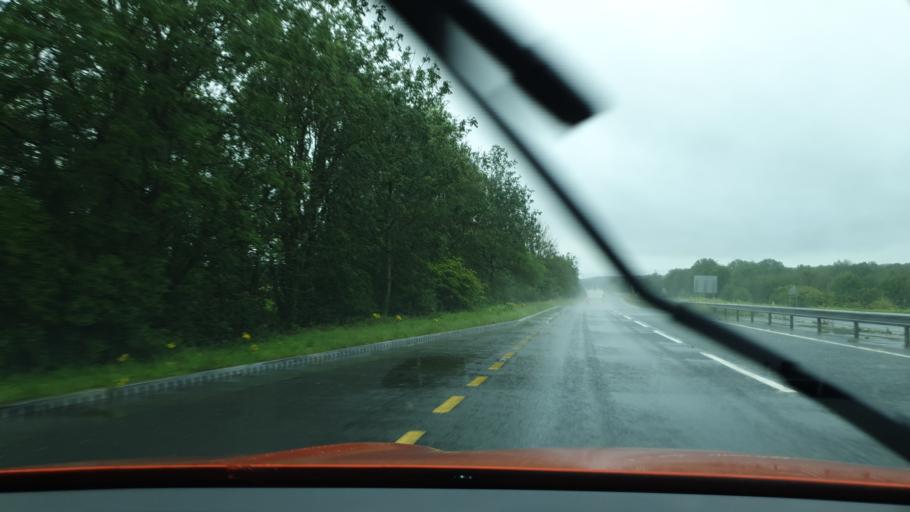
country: GB
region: England
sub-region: Cumbria
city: Arnside
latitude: 54.2377
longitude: -2.8570
